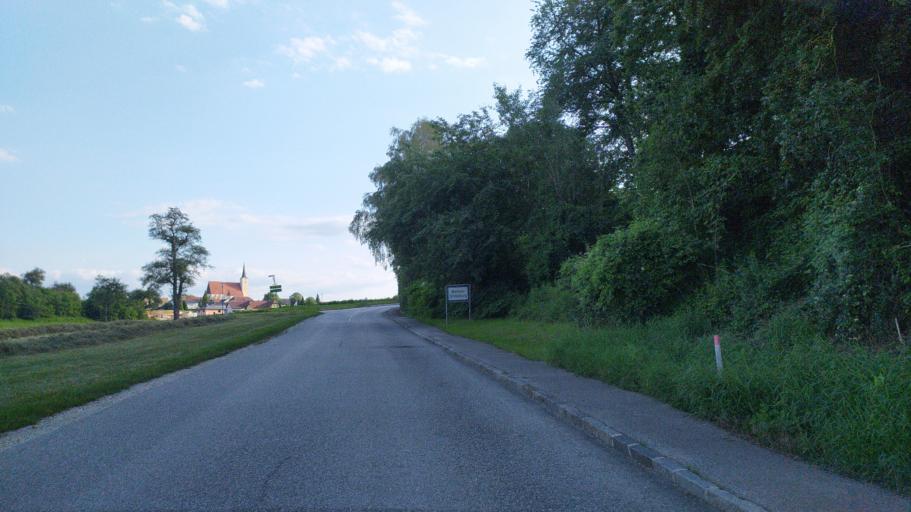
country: AT
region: Lower Austria
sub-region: Politischer Bezirk Amstetten
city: Zeillern
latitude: 48.1644
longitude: 14.7213
